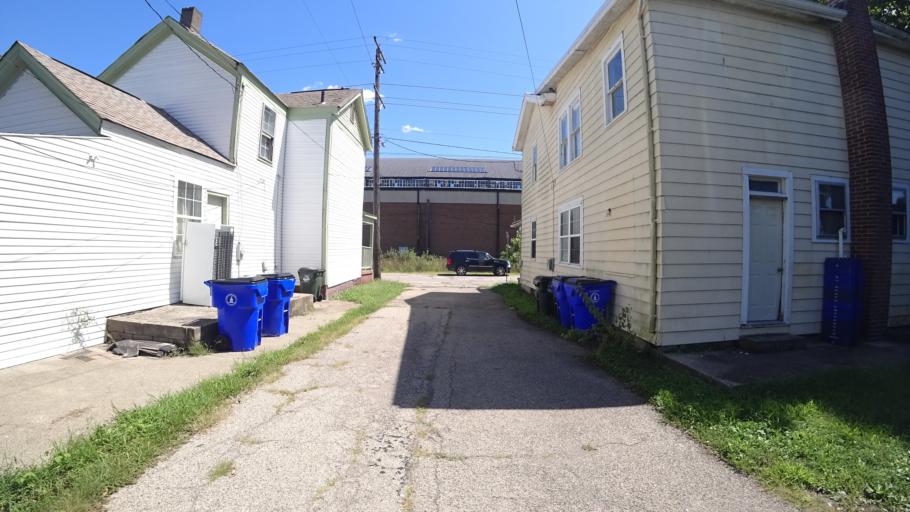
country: US
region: Ohio
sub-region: Butler County
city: Hamilton
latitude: 39.4041
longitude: -84.5566
